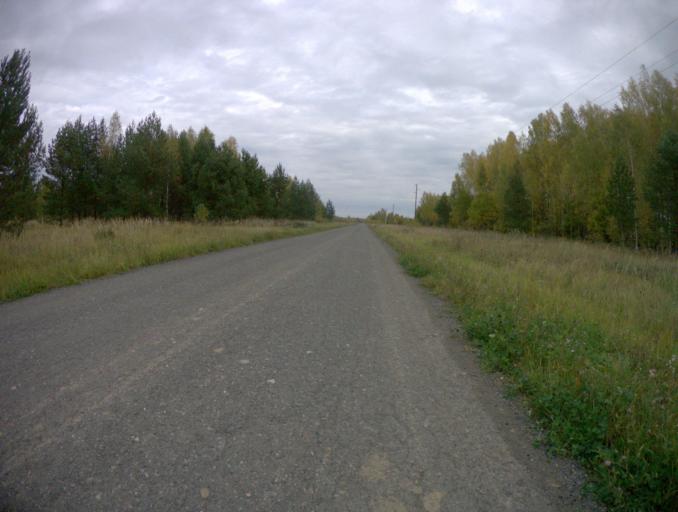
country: RU
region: Vladimir
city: Mstera
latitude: 56.3724
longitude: 41.8197
